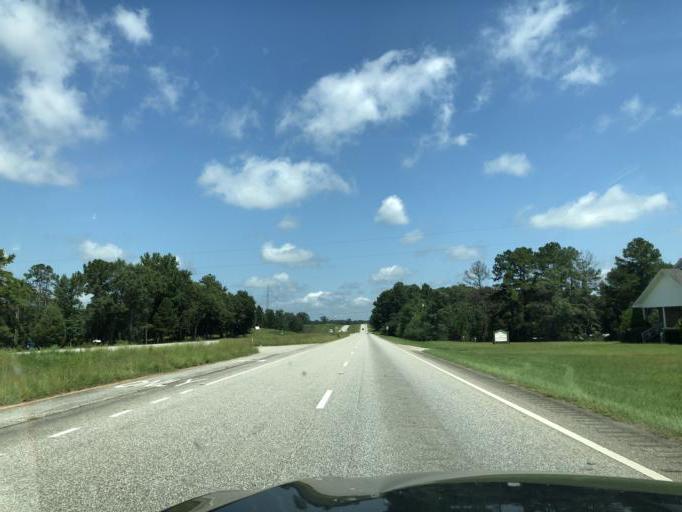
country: US
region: Alabama
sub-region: Henry County
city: Abbeville
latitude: 31.7032
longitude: -85.2764
